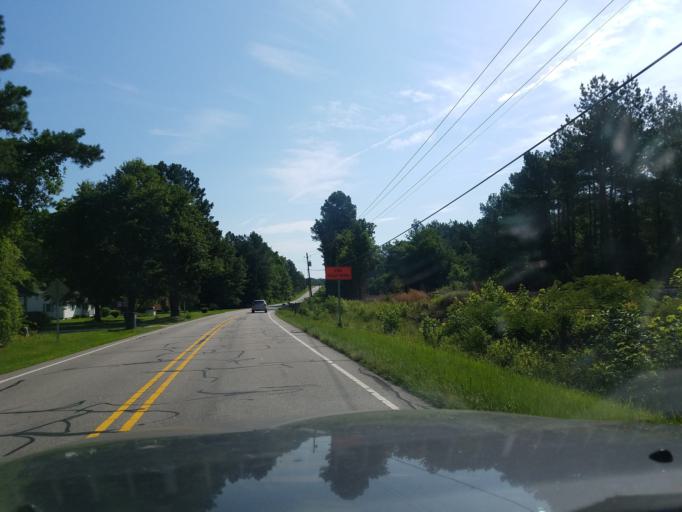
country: US
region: North Carolina
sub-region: Granville County
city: Oxford
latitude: 36.2843
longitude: -78.6318
